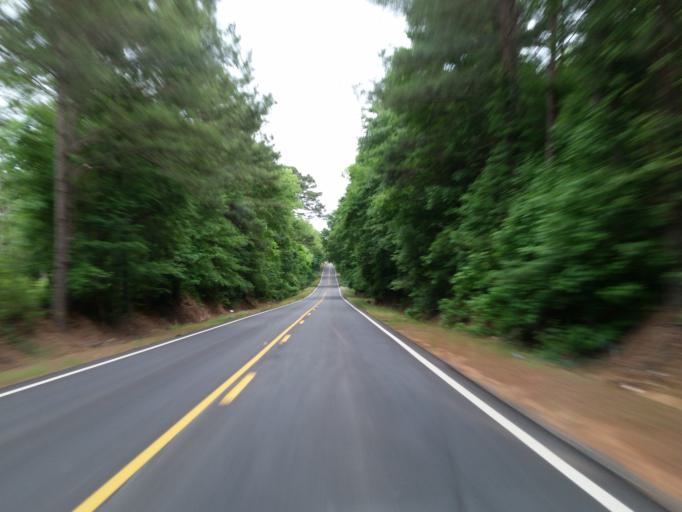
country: US
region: Georgia
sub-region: Dooly County
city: Unadilla
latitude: 32.3205
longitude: -83.7772
